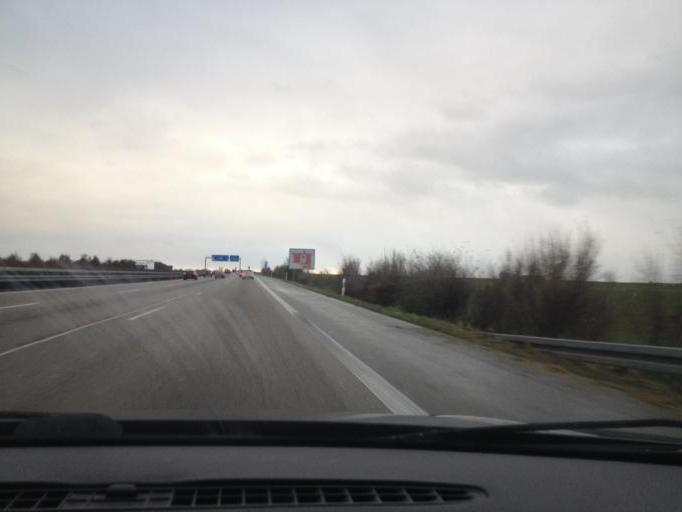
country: DE
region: Baden-Wuerttemberg
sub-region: Regierungsbezirk Stuttgart
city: Moglingen
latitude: 48.8661
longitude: 9.1306
